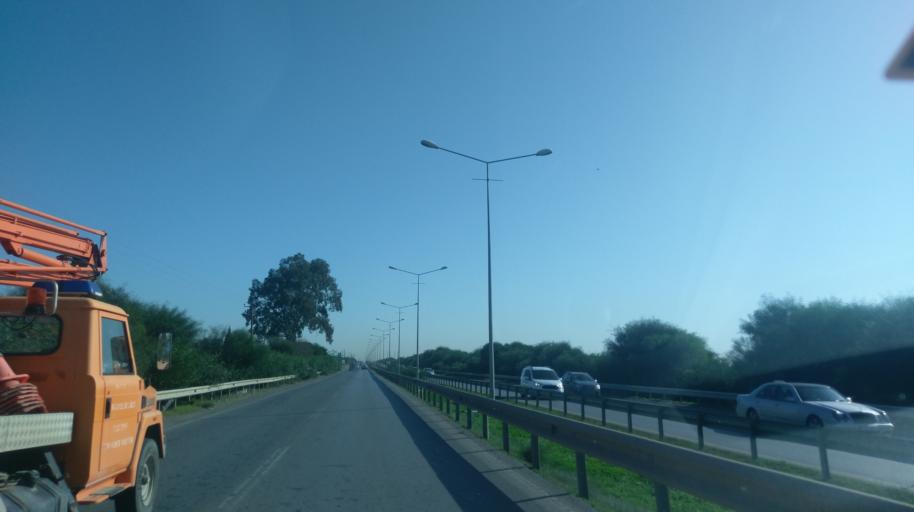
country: CY
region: Lefkosia
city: Nicosia
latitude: 35.2137
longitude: 33.3911
